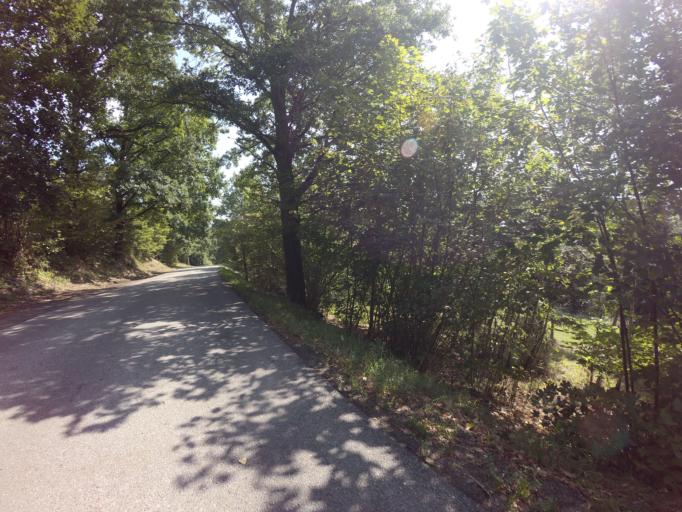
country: CZ
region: Jihocesky
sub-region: Okres Cesky Krumlov
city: Vyssi Brod
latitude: 48.6459
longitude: 14.3588
